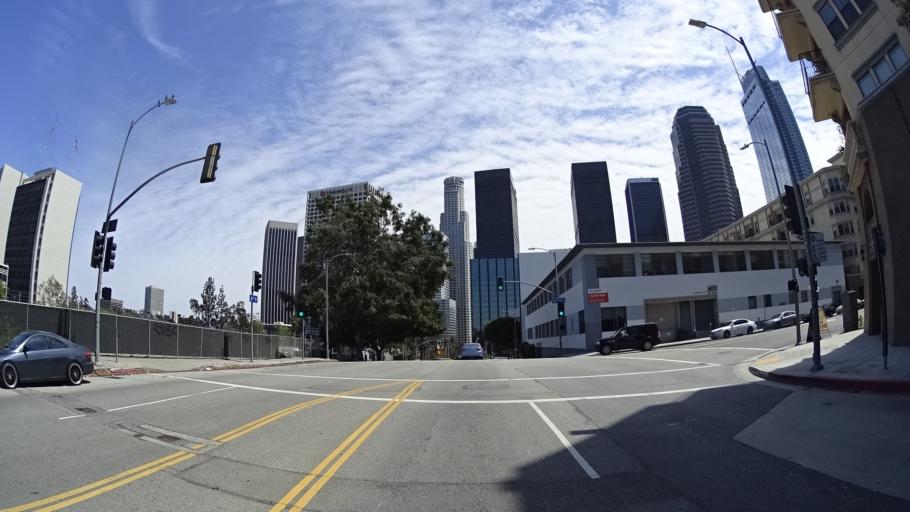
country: US
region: California
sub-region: Los Angeles County
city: Los Angeles
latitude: 34.0537
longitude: -118.2612
